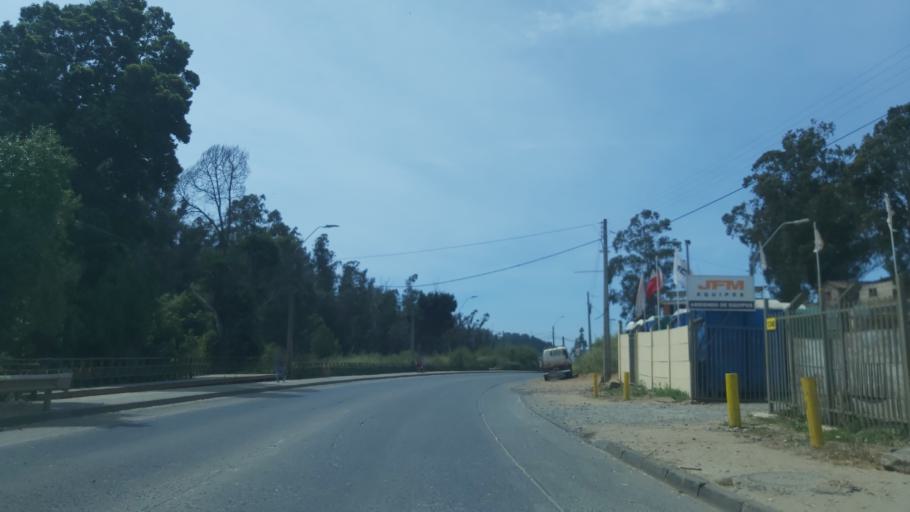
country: CL
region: Maule
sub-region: Provincia de Talca
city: Constitucion
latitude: -35.3390
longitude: -72.4205
